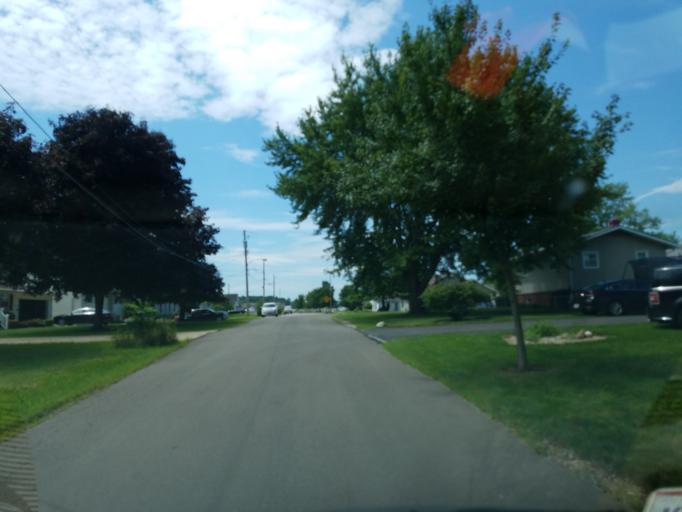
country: US
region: Ohio
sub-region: Ashland County
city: Ashland
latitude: 40.8659
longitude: -82.3344
